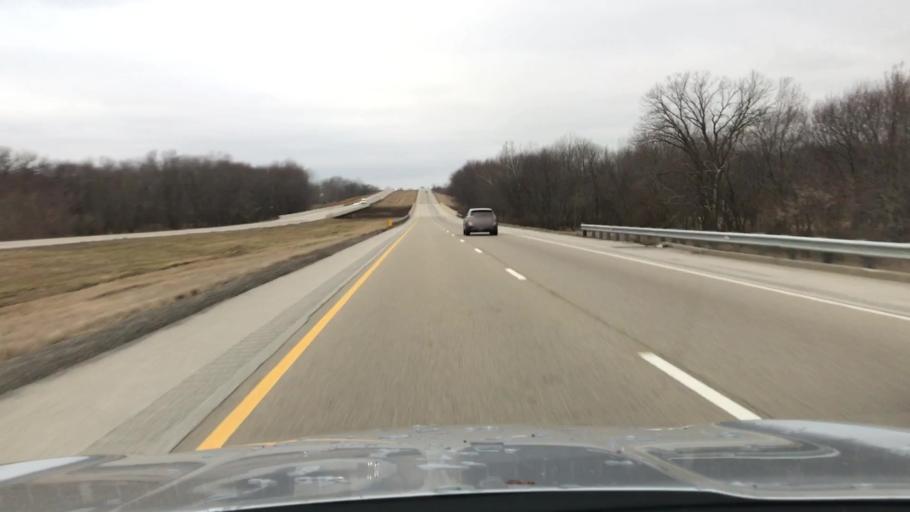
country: US
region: Illinois
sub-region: Logan County
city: Lincoln
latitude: 40.1809
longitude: -89.3662
